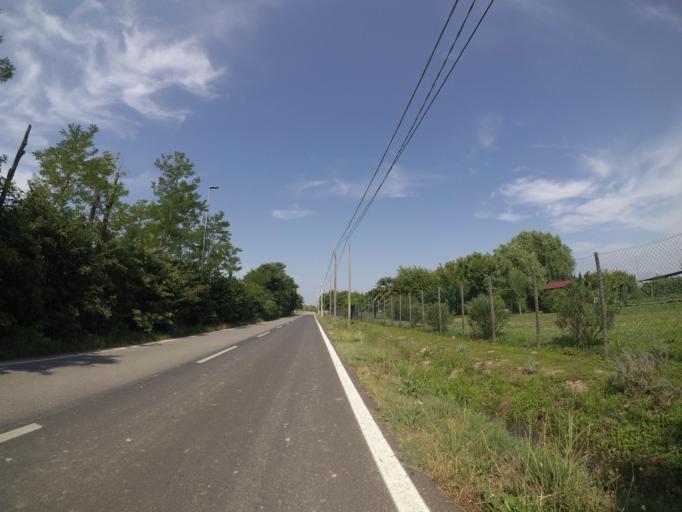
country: IT
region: Friuli Venezia Giulia
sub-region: Provincia di Pordenone
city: Rosa
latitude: 45.9097
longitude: 12.8881
